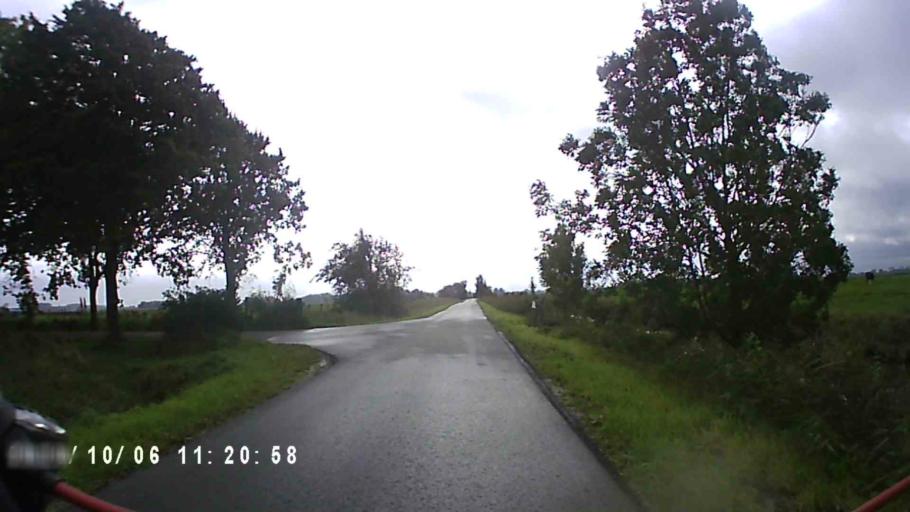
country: NL
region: Groningen
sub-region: Gemeente Zuidhorn
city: Oldehove
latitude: 53.3487
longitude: 6.4053
